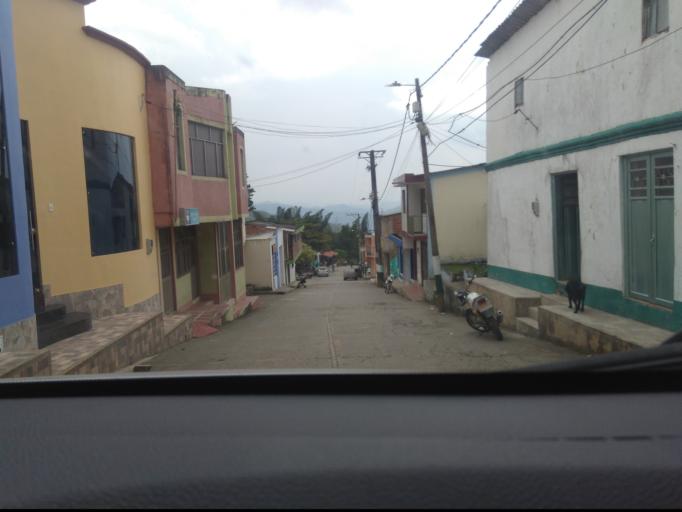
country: CO
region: Santander
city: Florian
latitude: 5.7307
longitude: -73.9327
